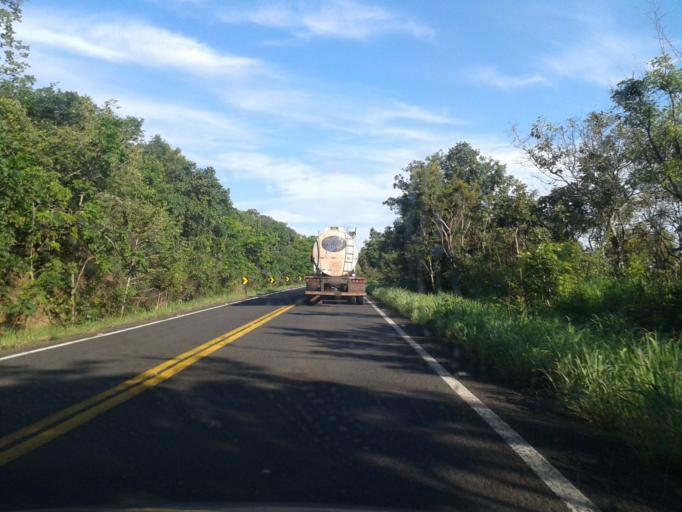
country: BR
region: Minas Gerais
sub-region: Tupaciguara
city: Tupaciguara
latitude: -18.2189
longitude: -48.5740
